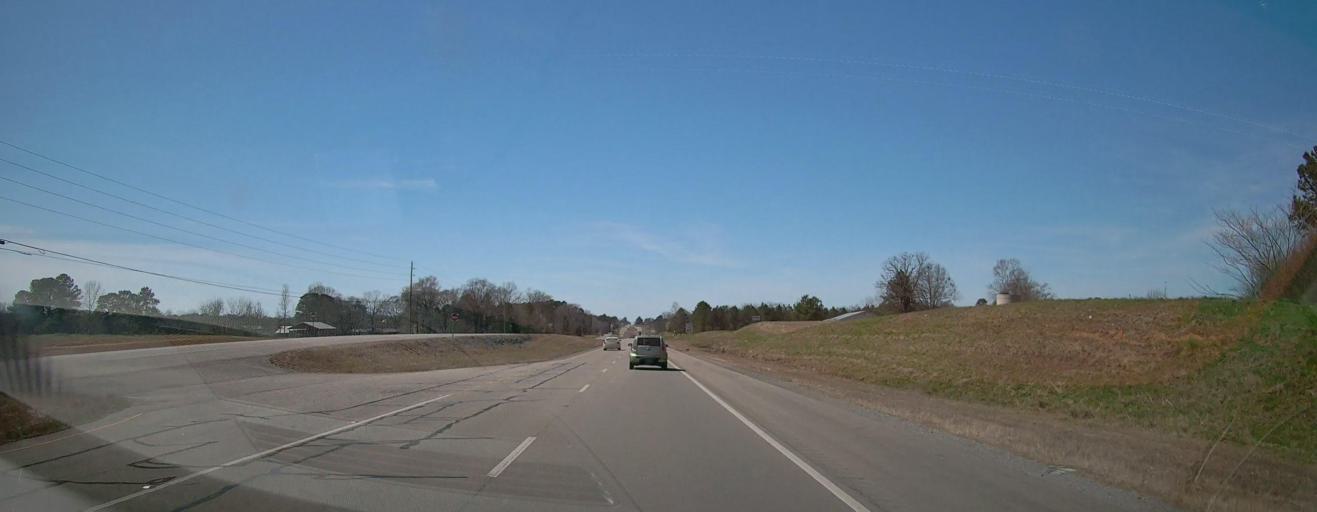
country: US
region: Alabama
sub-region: Cullman County
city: Hanceville
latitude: 34.1755
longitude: -86.7160
